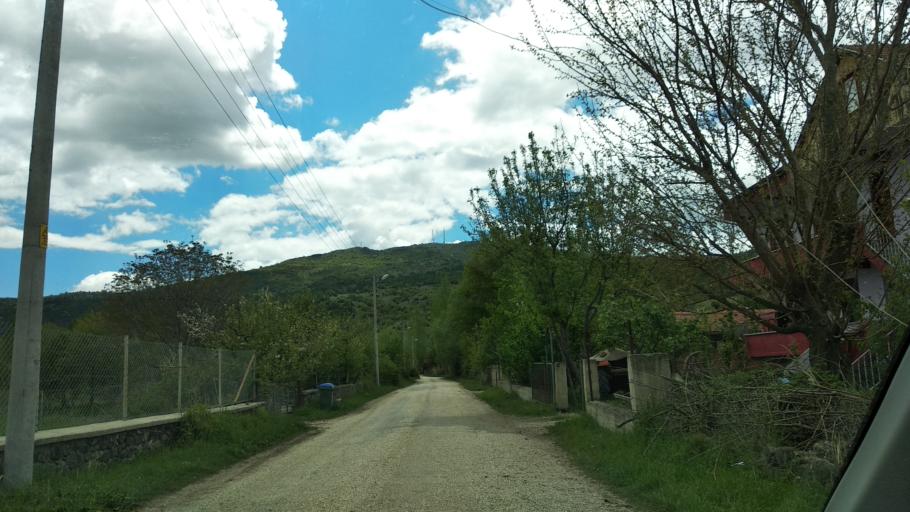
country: TR
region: Bolu
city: Seben
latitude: 40.4058
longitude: 31.5731
